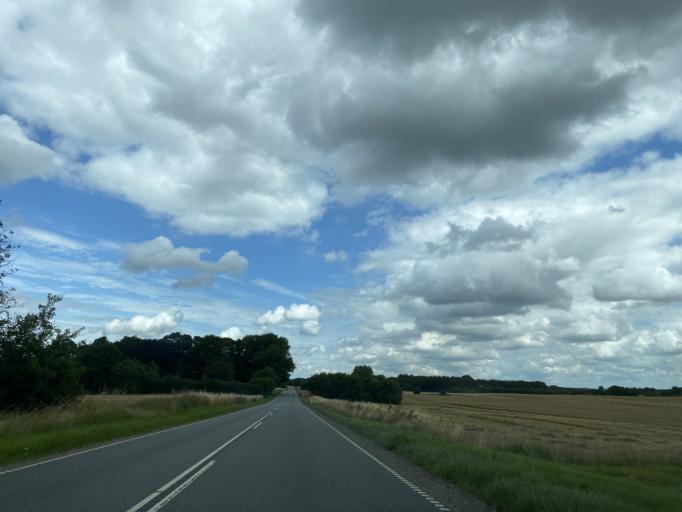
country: DK
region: Central Jutland
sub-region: Silkeborg Kommune
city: Silkeborg
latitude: 56.2409
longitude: 9.6238
